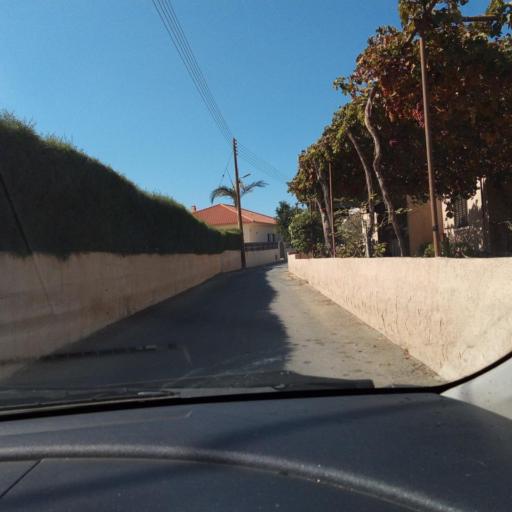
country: CY
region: Larnaka
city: Kolossi
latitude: 34.6005
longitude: 32.9540
